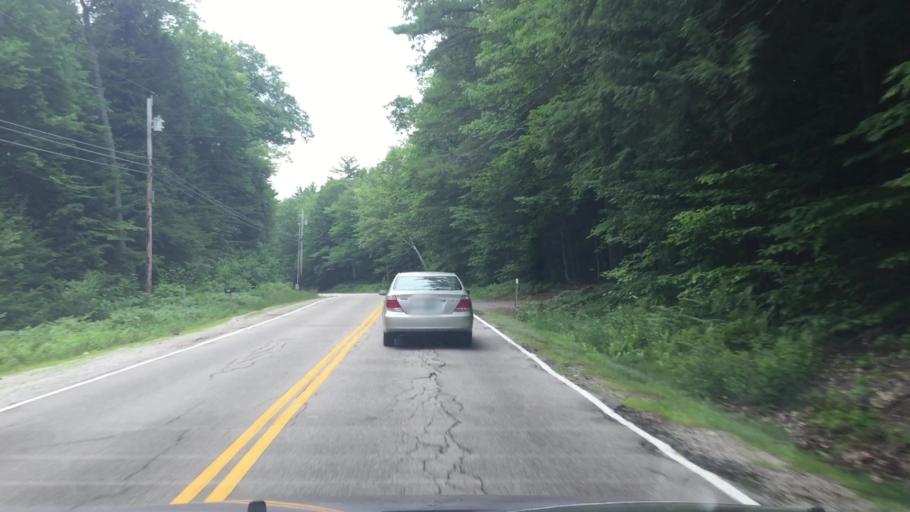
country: US
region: New Hampshire
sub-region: Carroll County
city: Conway
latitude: 43.9330
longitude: -71.0870
